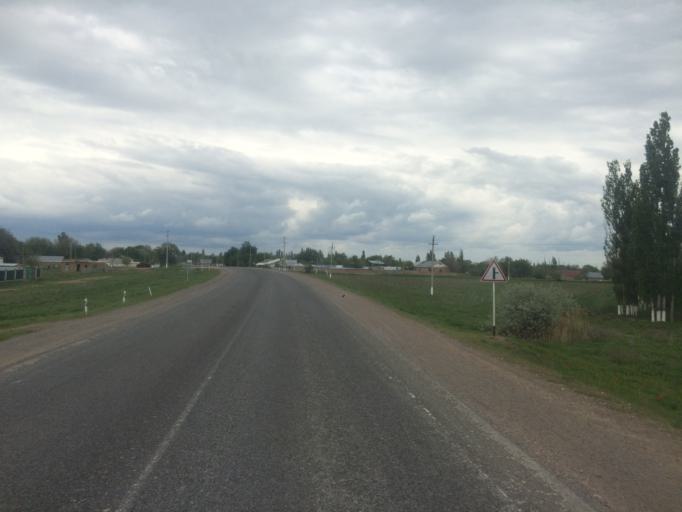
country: KZ
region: Zhambyl
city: Georgiyevka
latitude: 43.2284
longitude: 74.3844
